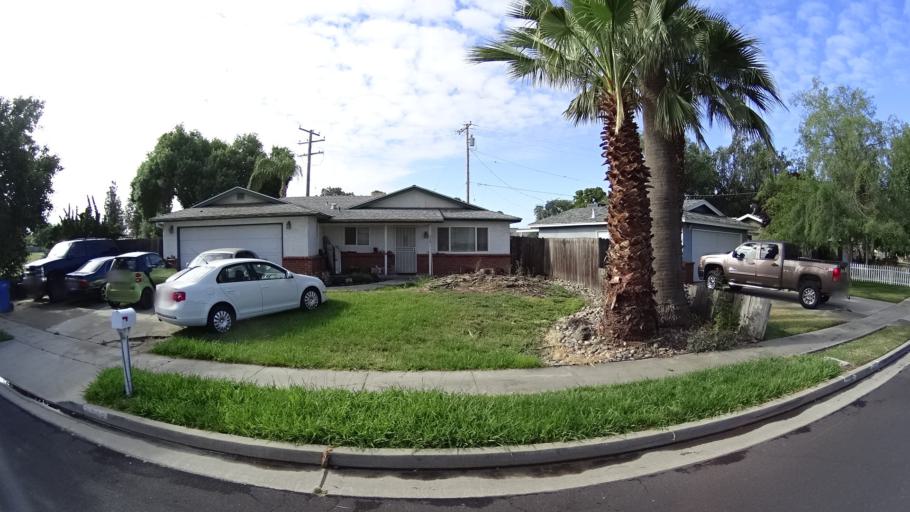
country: US
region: California
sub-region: Kings County
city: Lucerne
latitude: 36.3618
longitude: -119.6418
